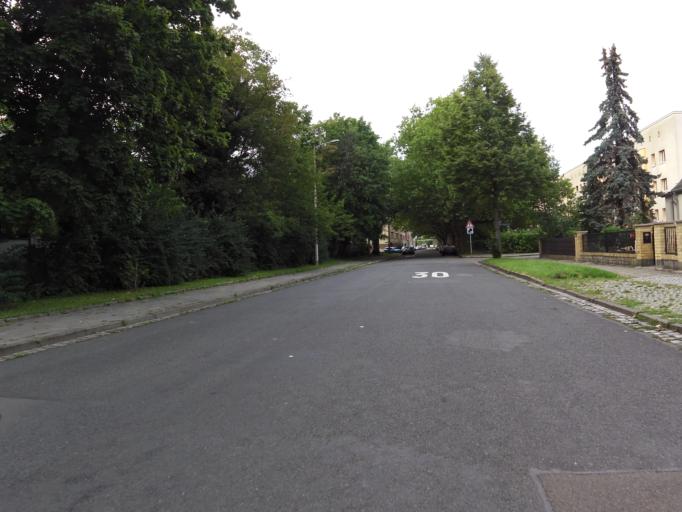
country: DE
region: Saxony
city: Taucha
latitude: 51.3480
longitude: 12.4394
